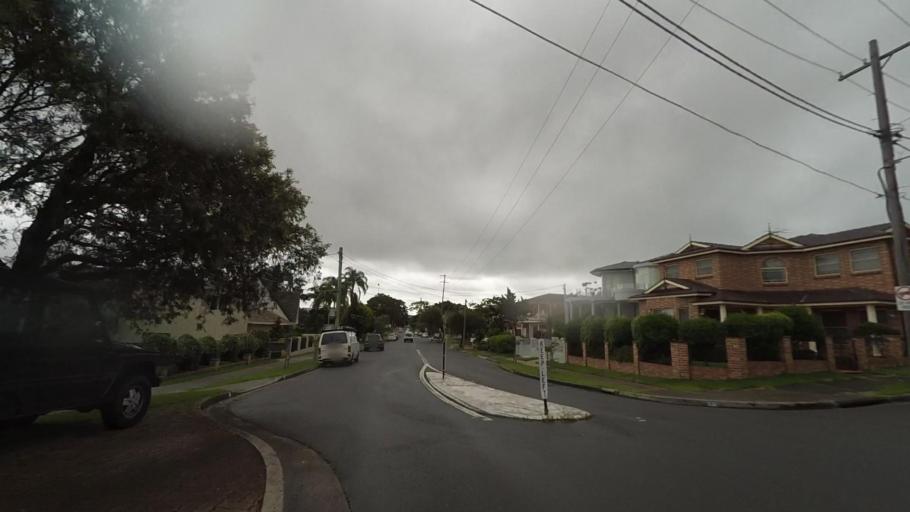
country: AU
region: New South Wales
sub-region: Rockdale
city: Ramsgate
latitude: -33.9863
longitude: 151.1318
